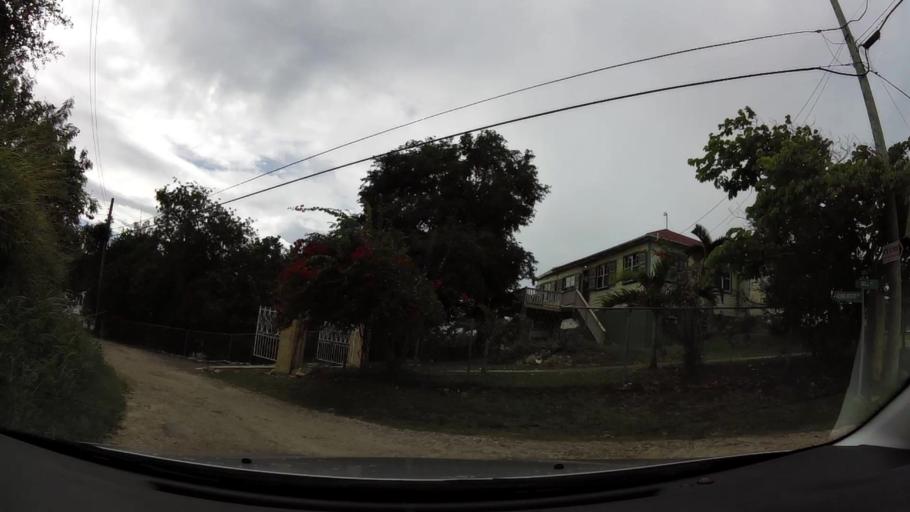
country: AG
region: Saint John
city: Potters Village
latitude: 17.0899
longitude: -61.8107
